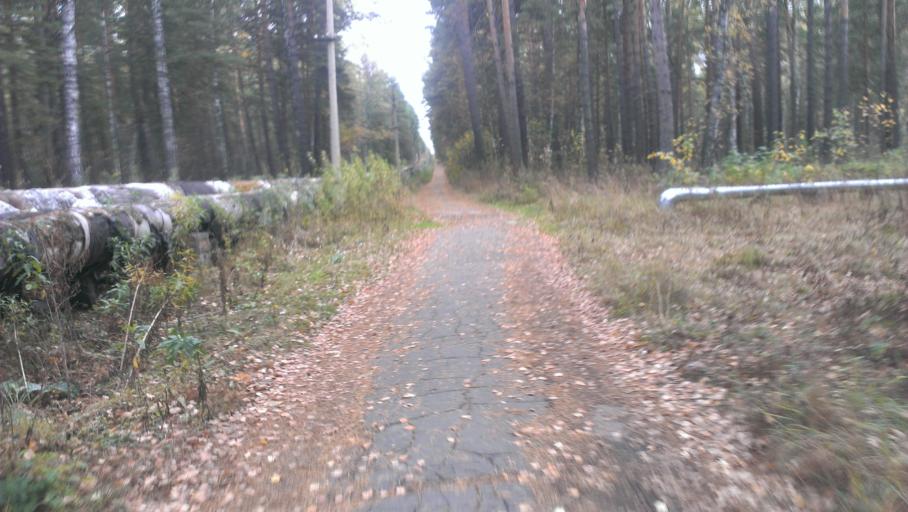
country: RU
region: Altai Krai
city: Yuzhnyy
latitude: 53.2686
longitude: 83.6821
